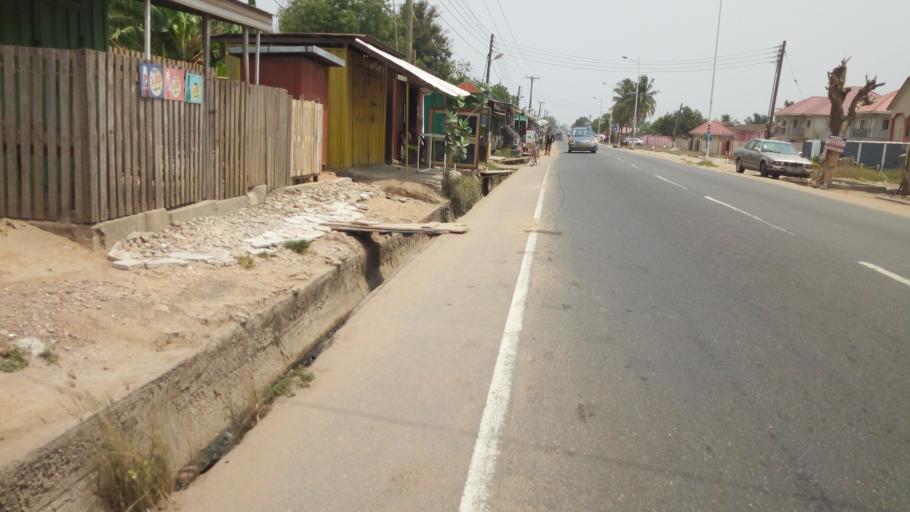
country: GH
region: Greater Accra
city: Gbawe
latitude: 5.5584
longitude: -0.3095
